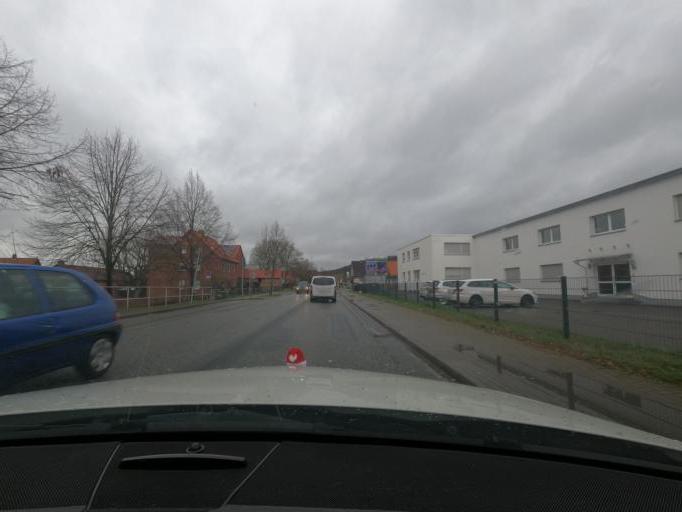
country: DE
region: Lower Saxony
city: Northeim
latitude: 51.7619
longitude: 9.9618
